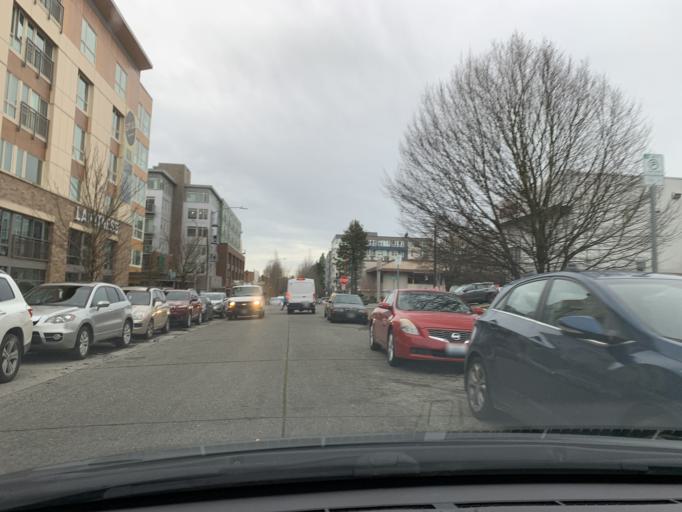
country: US
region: Washington
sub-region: King County
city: White Center
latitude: 47.5616
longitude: -122.3828
